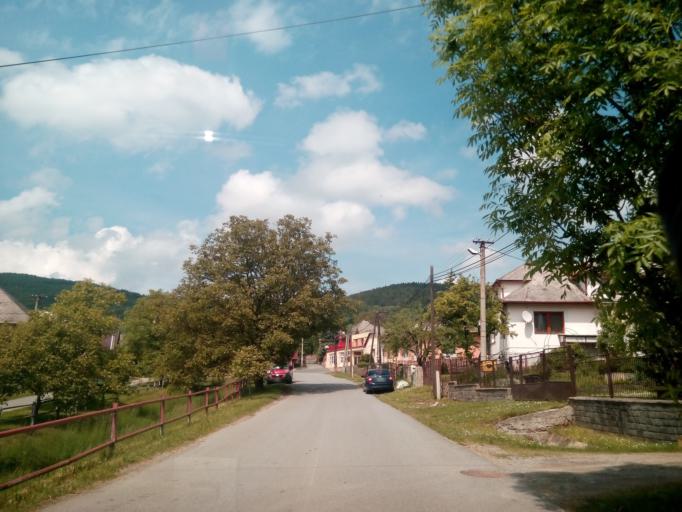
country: SK
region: Presovsky
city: Lipany
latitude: 49.0551
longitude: 20.9526
